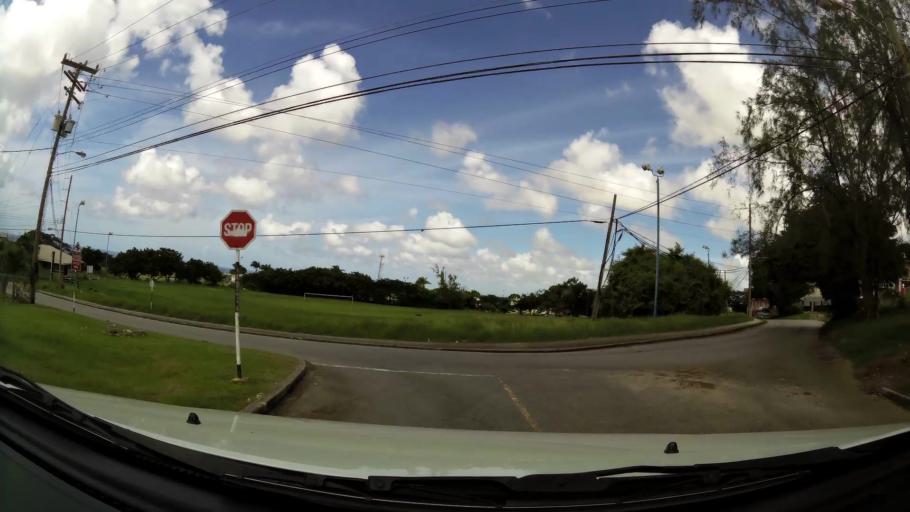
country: BB
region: Saint James
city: Holetown
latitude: 13.1533
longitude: -59.6272
